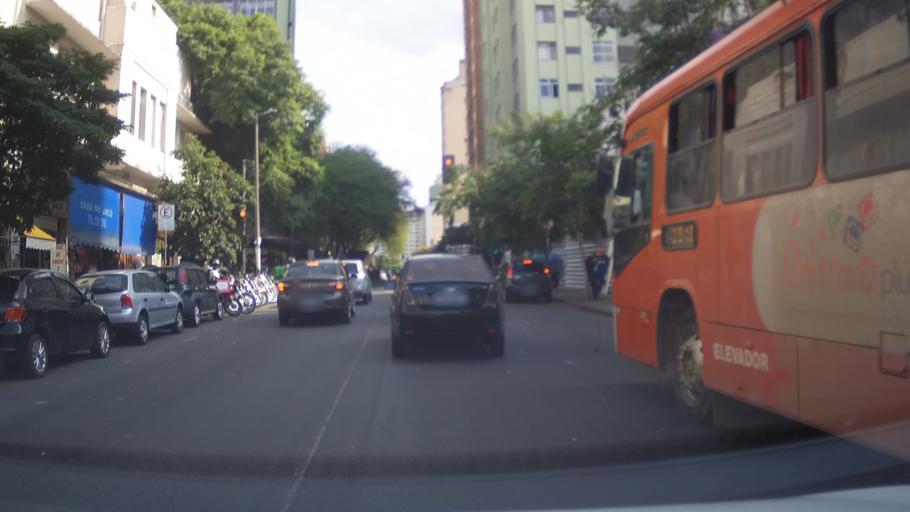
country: BR
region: Minas Gerais
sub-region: Belo Horizonte
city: Belo Horizonte
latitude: -19.9165
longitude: -43.9425
